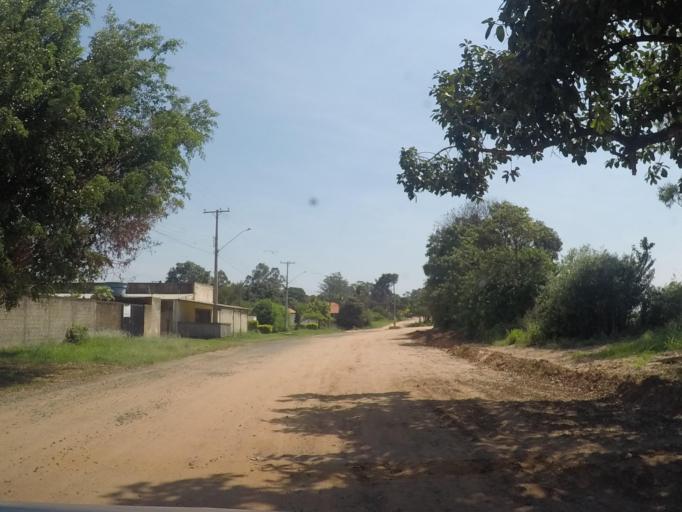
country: BR
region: Sao Paulo
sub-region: Sumare
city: Sumare
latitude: -22.8801
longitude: -47.2893
